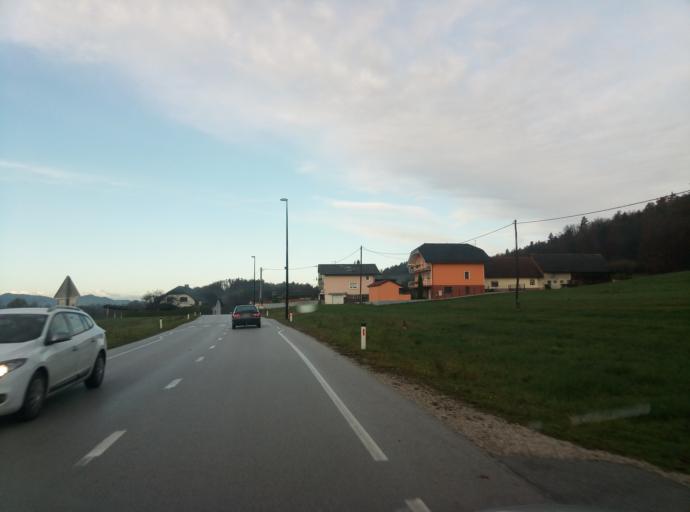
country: SI
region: Komenda
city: Moste
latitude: 46.1683
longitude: 14.5376
